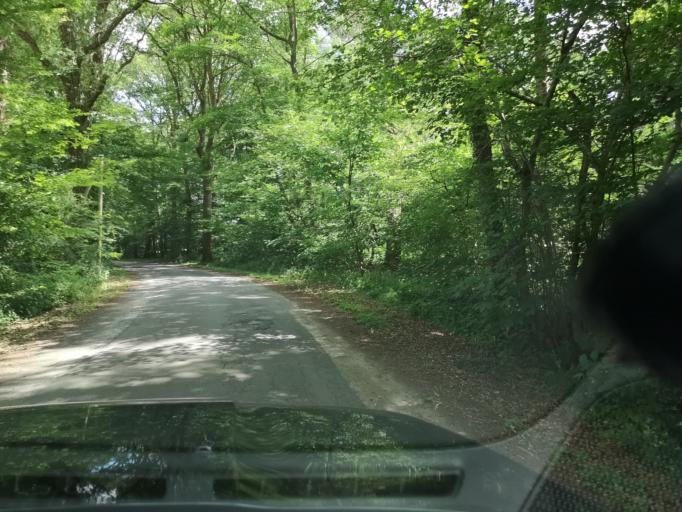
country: DE
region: North Rhine-Westphalia
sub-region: Regierungsbezirk Munster
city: Rhede
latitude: 51.8555
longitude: 6.6842
